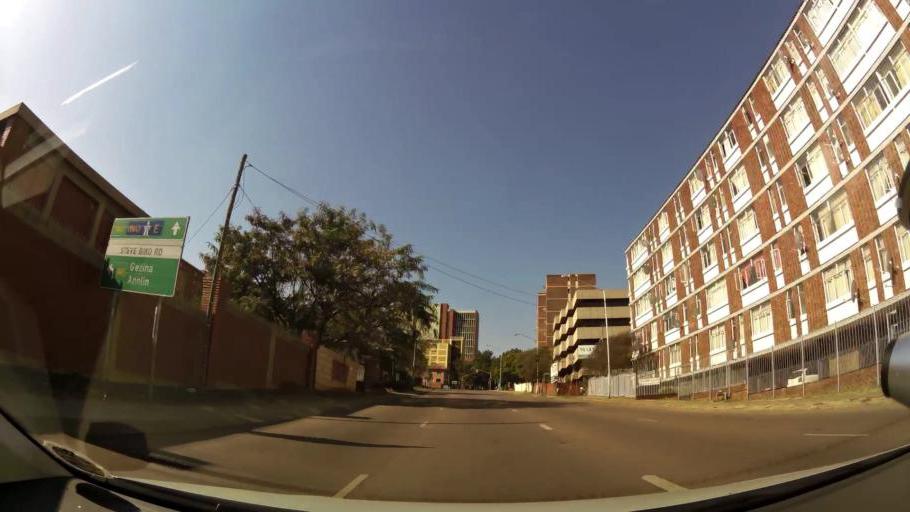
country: ZA
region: Gauteng
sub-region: City of Tshwane Metropolitan Municipality
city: Pretoria
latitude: -25.7411
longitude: 28.2022
